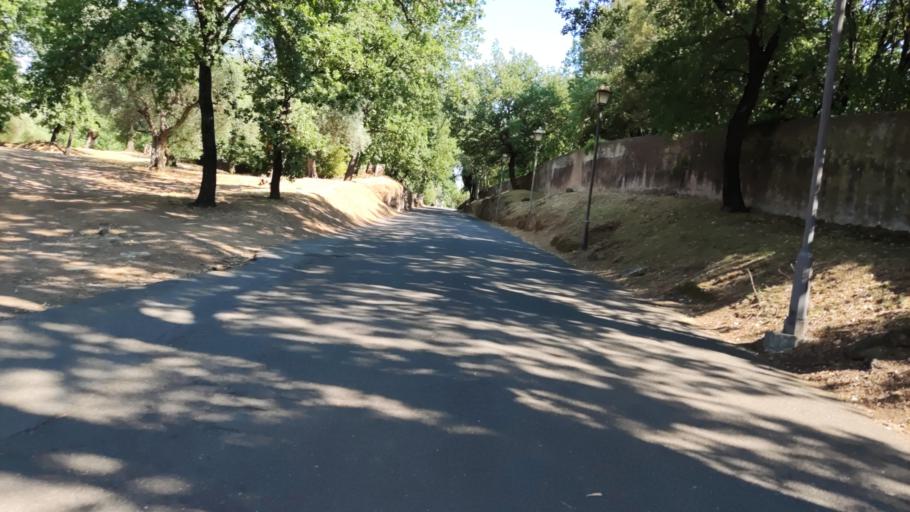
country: IT
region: Latium
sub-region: Citta metropolitana di Roma Capitale
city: Villa Adriana
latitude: 41.9444
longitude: 12.7725
